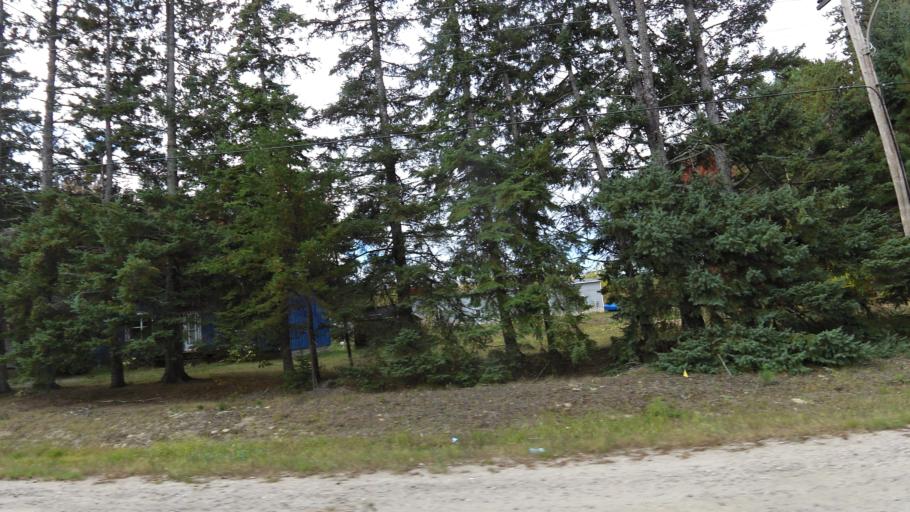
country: CA
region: Ontario
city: Deep River
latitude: 46.0896
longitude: -77.4907
